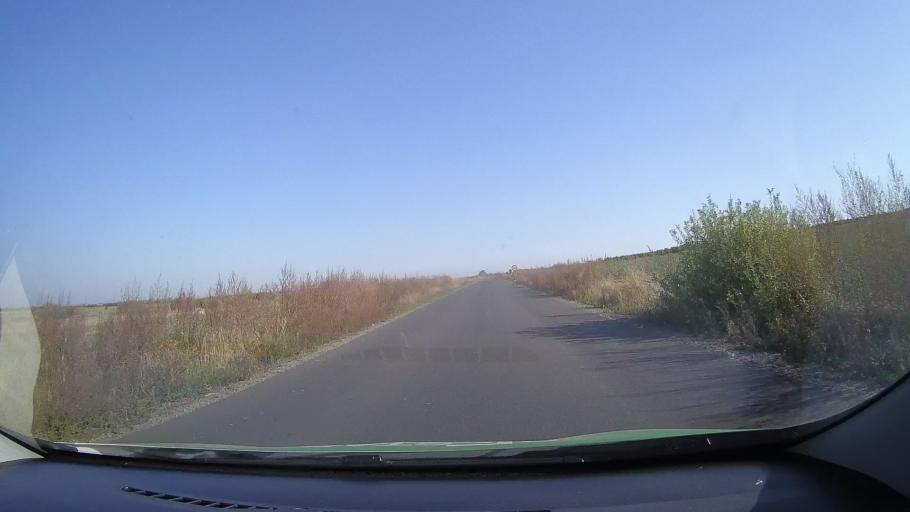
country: RO
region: Satu Mare
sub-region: Comuna Sauca
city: Sauca
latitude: 47.4897
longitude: 22.4667
